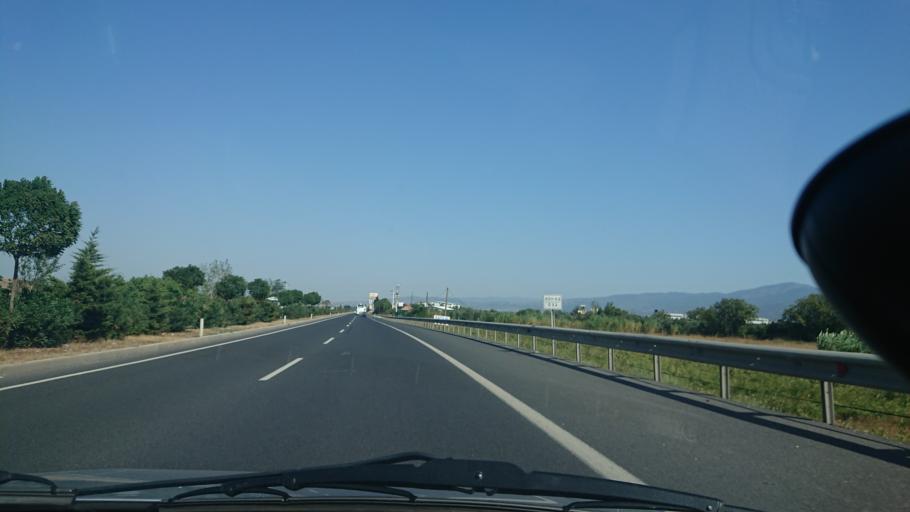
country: TR
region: Manisa
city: Karaoglanli
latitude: 38.4471
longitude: 27.5240
